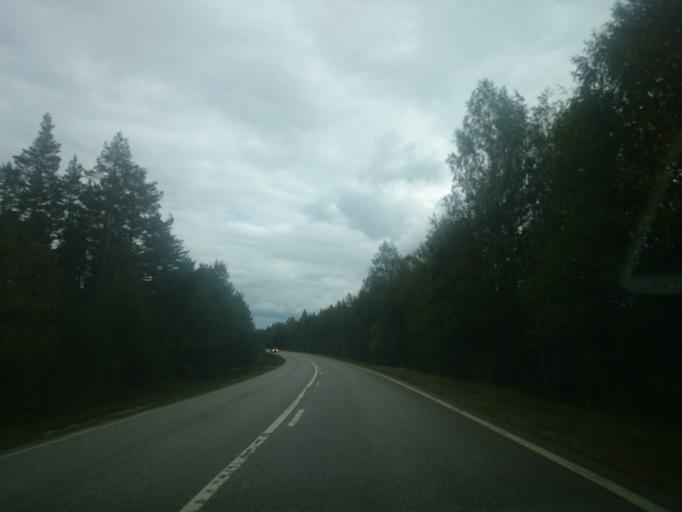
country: SE
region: Jaemtland
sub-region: Harjedalens Kommun
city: Sveg
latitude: 62.1244
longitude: 14.0777
